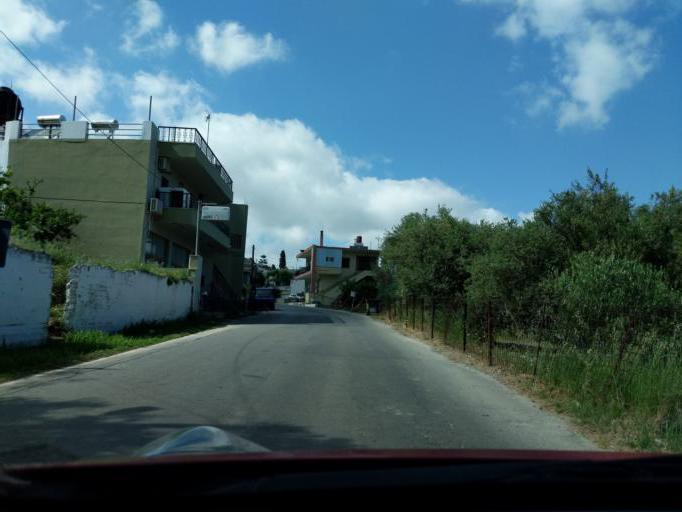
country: GR
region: Crete
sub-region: Nomos Chanias
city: Kissamos
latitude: 35.4244
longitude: 23.6865
